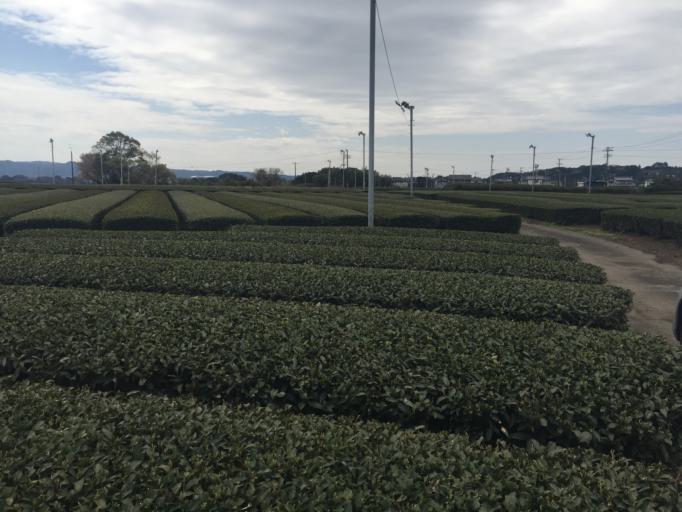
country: JP
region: Shizuoka
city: Mori
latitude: 34.7970
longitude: 137.9499
